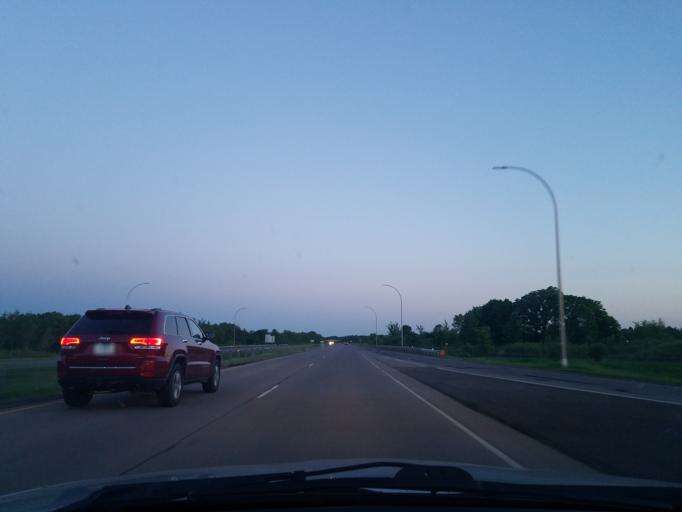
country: US
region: Minnesota
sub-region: Chisago County
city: Rush City
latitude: 45.6825
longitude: -92.9894
